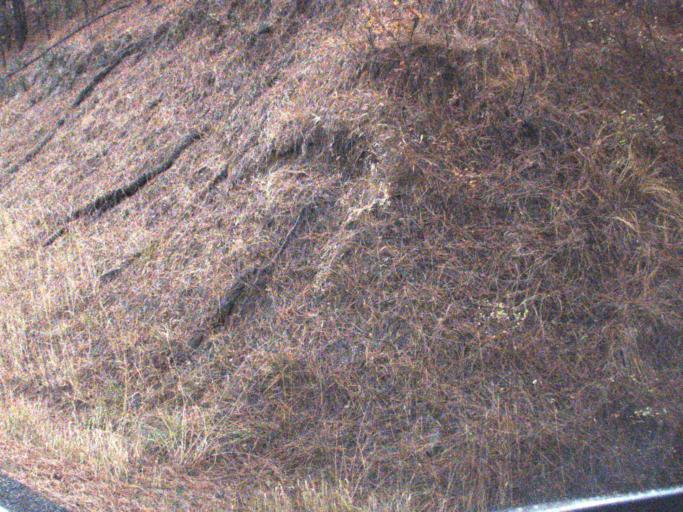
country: US
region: Washington
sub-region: Stevens County
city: Kettle Falls
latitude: 48.2771
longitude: -118.1355
